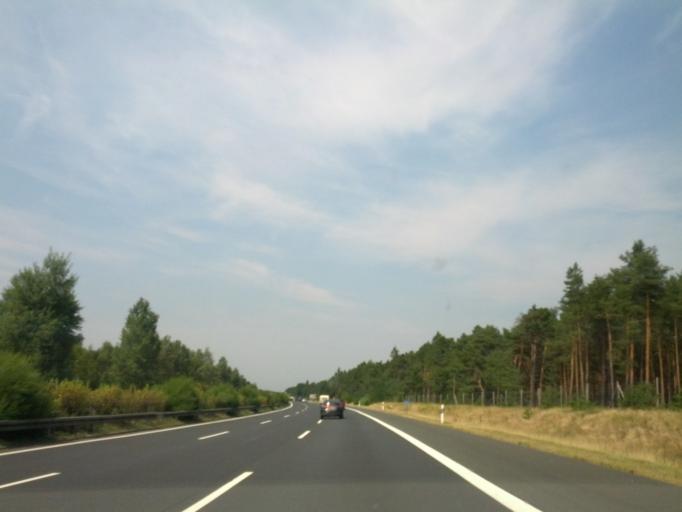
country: DE
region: Brandenburg
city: Fichtenwalde
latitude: 52.2416
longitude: 12.9171
